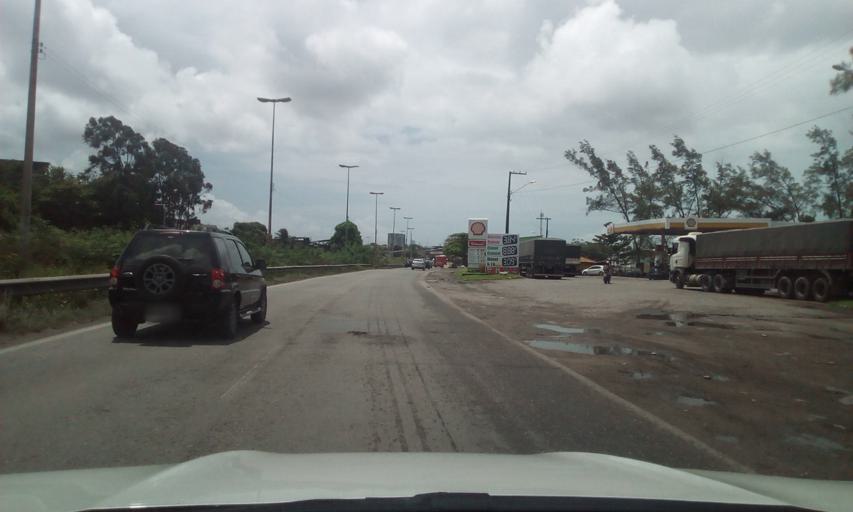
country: BR
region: Pernambuco
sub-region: Recife
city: Recife
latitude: -8.0858
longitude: -34.9458
